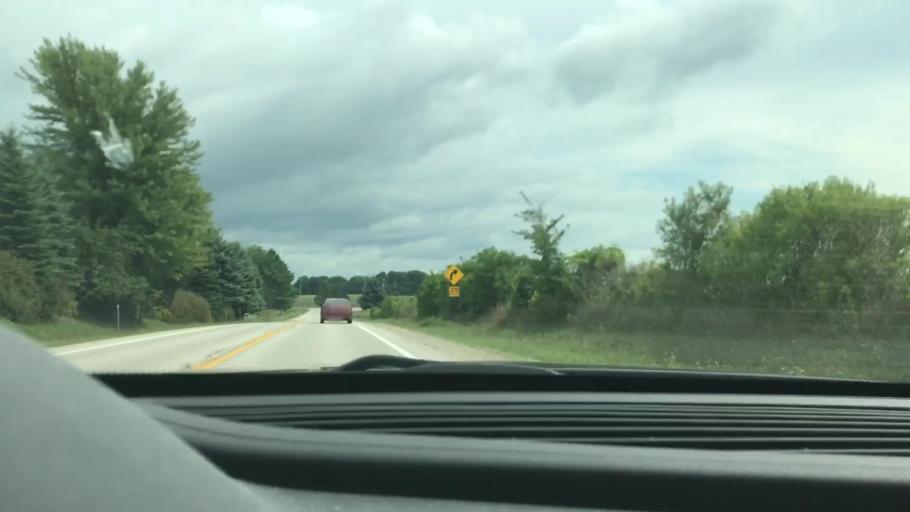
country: US
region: Michigan
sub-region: Antrim County
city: Bellaire
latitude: 45.0941
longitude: -85.2935
